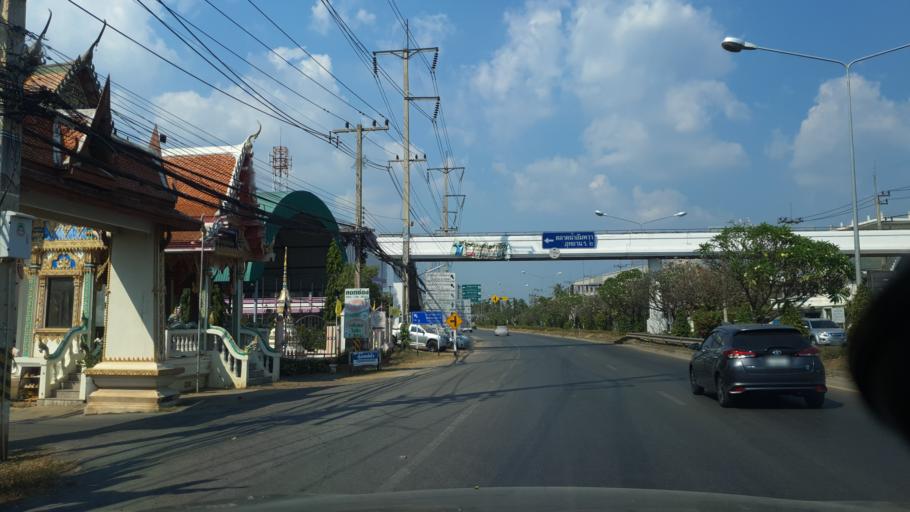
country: TH
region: Samut Songkhram
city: Amphawa
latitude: 13.4203
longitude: 99.9633
